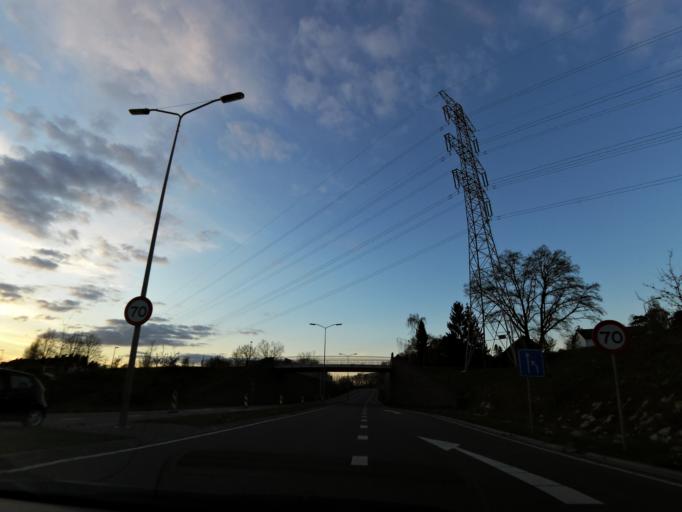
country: NL
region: Limburg
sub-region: Gemeente Heerlen
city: Heerlen
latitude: 50.9030
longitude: 5.9949
